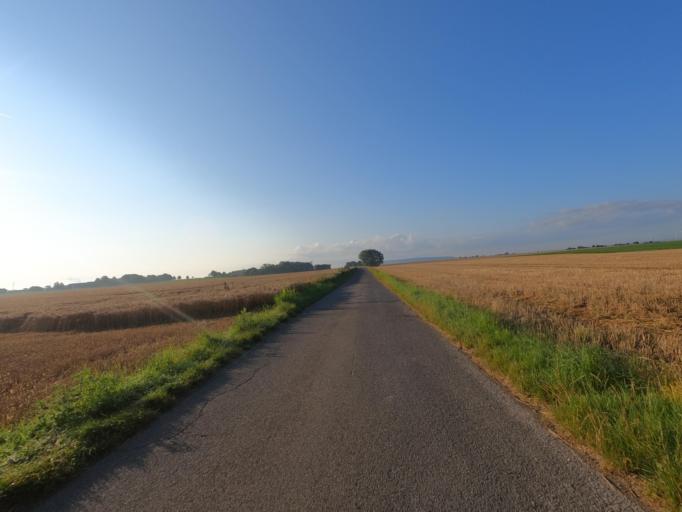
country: DE
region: North Rhine-Westphalia
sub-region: Regierungsbezirk Koln
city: Titz
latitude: 51.0201
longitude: 6.3569
